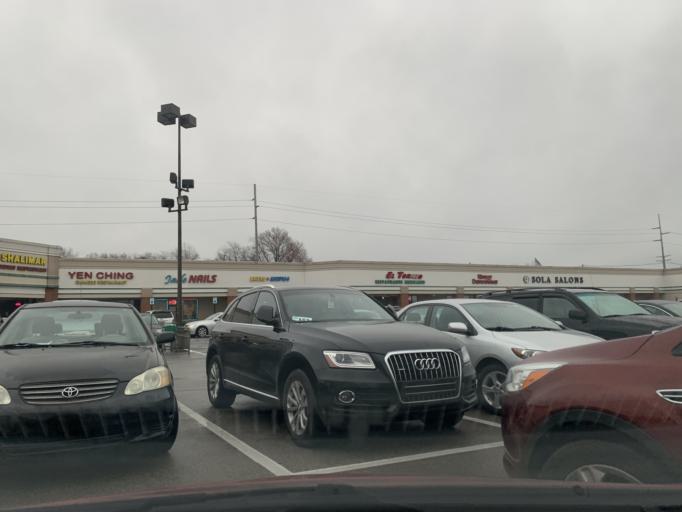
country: US
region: Kentucky
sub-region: Jefferson County
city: Hurstbourne Acres
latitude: 38.2212
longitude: -85.5840
